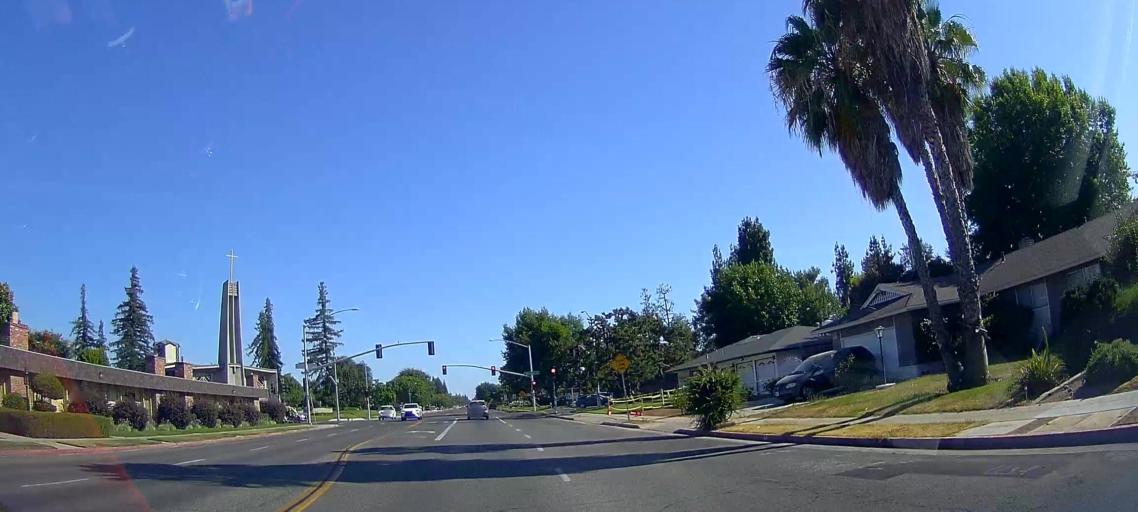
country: US
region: California
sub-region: Fresno County
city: Fresno
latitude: 36.8235
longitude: -119.7994
